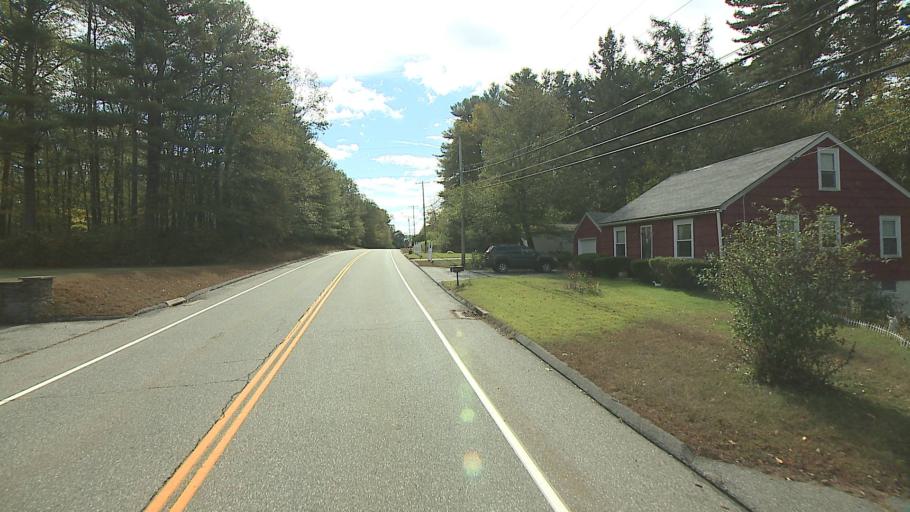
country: US
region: Connecticut
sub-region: Windham County
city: North Grosvenor Dale
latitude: 41.9984
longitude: -71.8991
